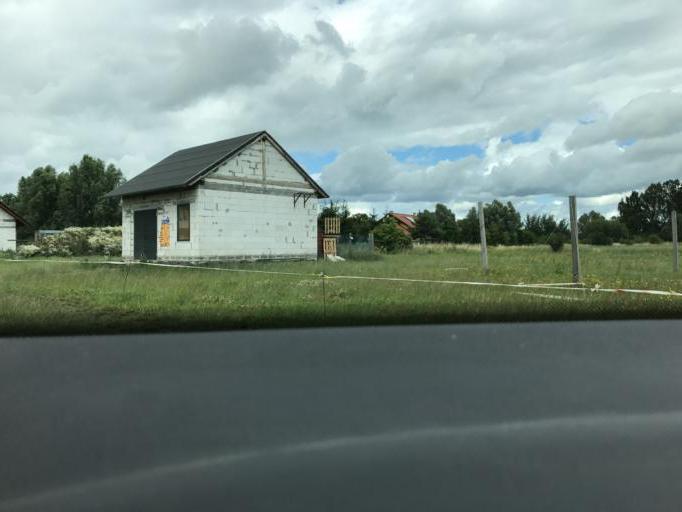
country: PL
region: Pomeranian Voivodeship
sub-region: Powiat gdanski
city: Pruszcz Gdanski
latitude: 54.2708
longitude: 18.6844
